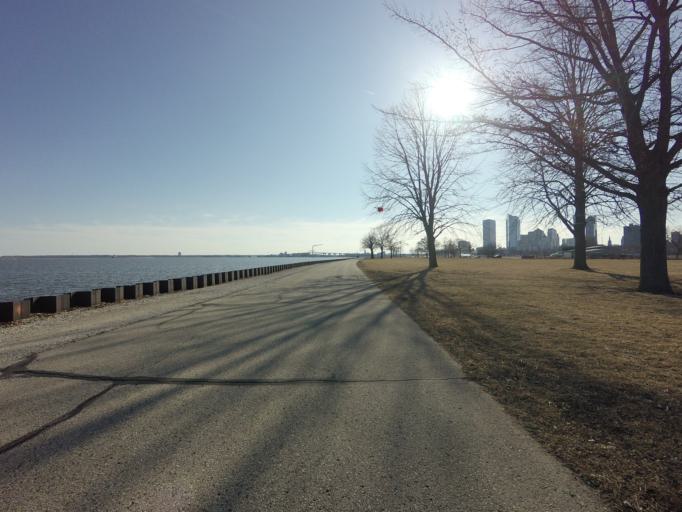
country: US
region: Wisconsin
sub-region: Milwaukee County
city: Milwaukee
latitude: 43.0456
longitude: -87.8848
